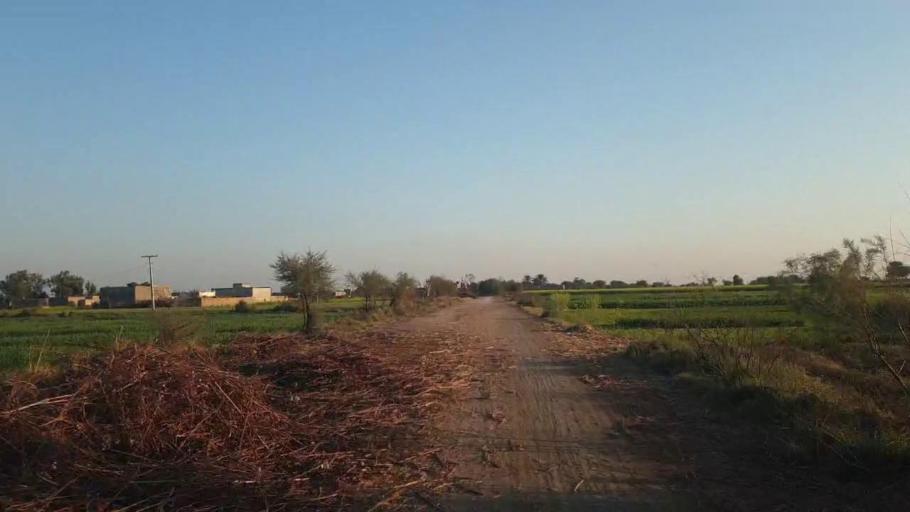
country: PK
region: Sindh
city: Khadro
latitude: 26.0754
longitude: 68.6893
